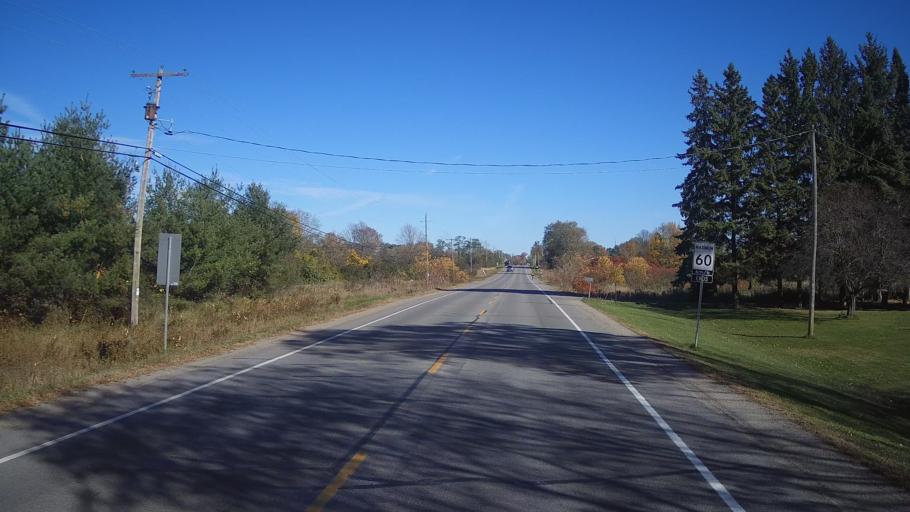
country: CA
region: Ontario
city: Kingston
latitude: 44.4073
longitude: -76.5694
